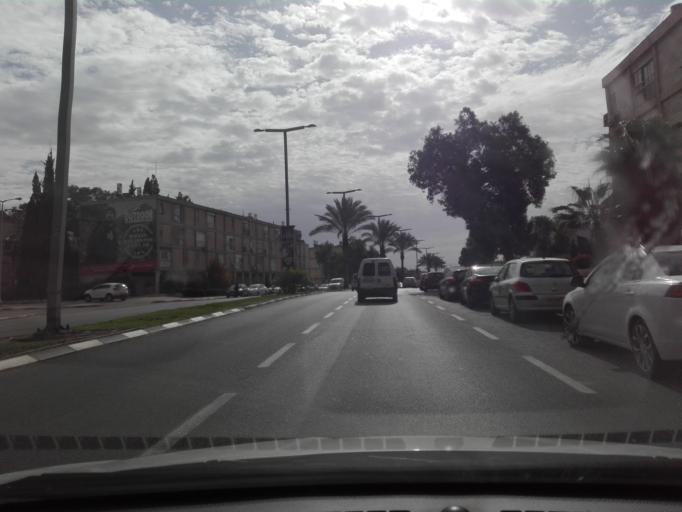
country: IL
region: Southern District
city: Beersheba
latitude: 31.2721
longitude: 34.7979
